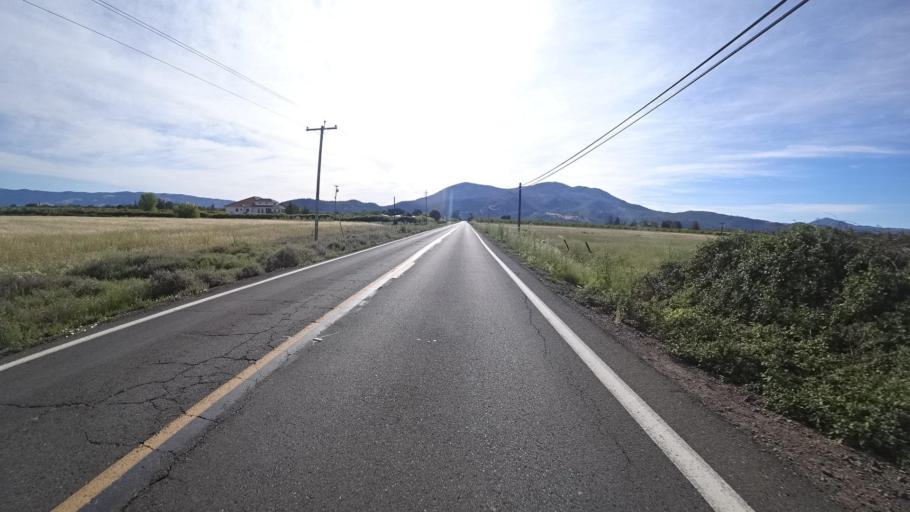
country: US
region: California
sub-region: Lake County
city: Kelseyville
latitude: 38.9893
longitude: -122.8545
